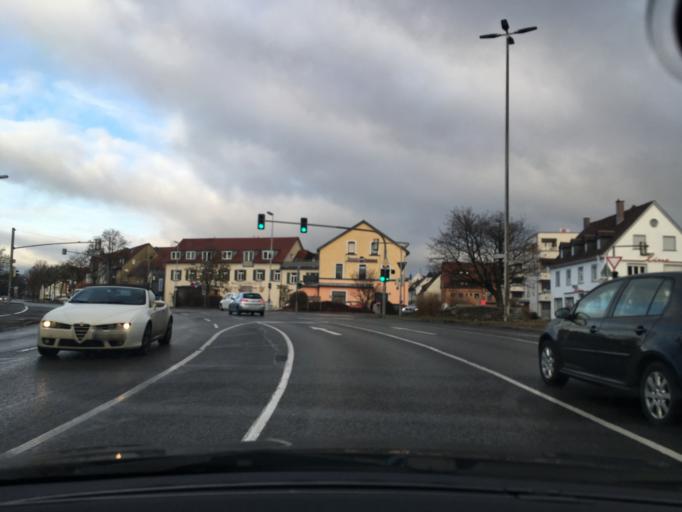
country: DE
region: Baden-Wuerttemberg
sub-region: Tuebingen Region
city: Weingarten
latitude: 47.8036
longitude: 9.6363
